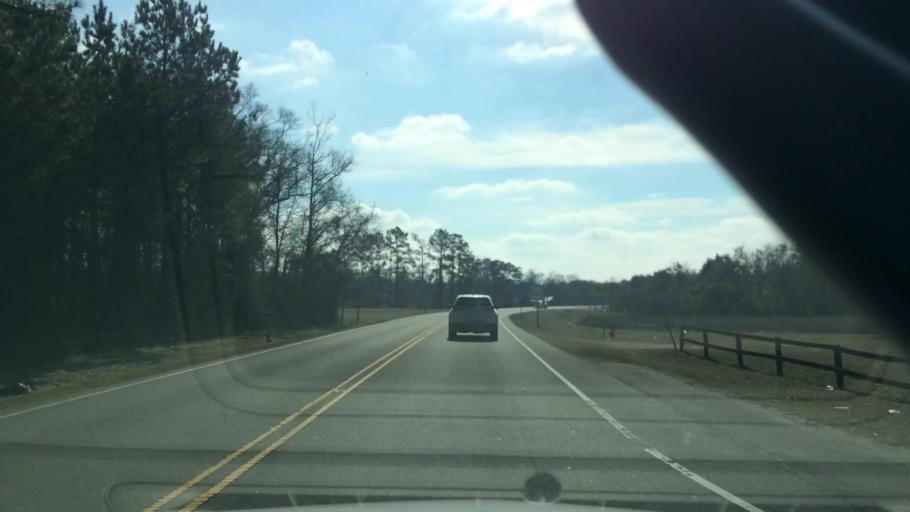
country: US
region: North Carolina
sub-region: Duplin County
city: Beulaville
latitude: 34.8235
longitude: -77.8392
